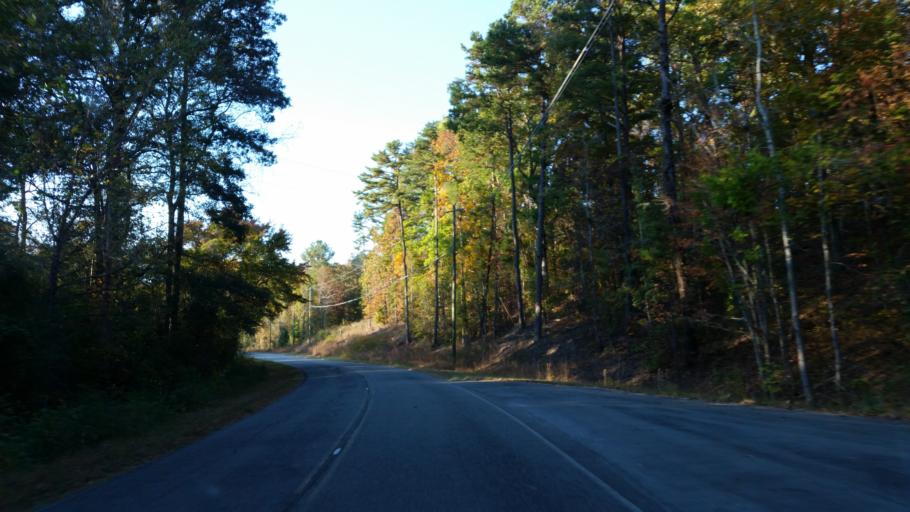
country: US
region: Georgia
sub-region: Bartow County
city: Euharlee
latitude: 34.2235
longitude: -84.9360
